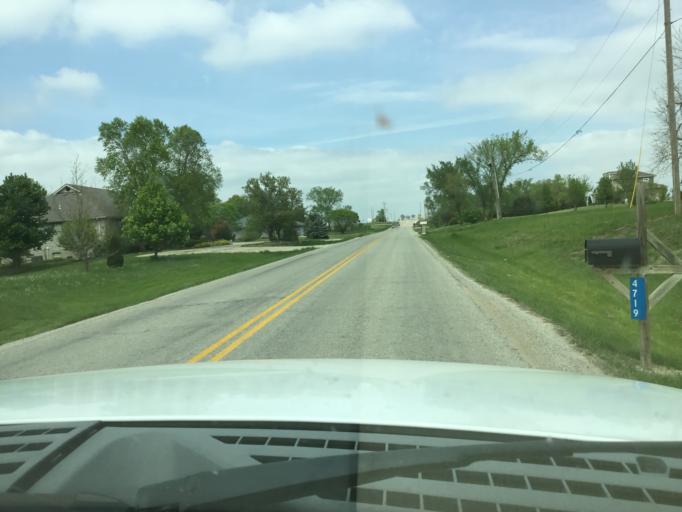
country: US
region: Kansas
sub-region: Shawnee County
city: Topeka
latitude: 38.9823
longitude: -95.6144
